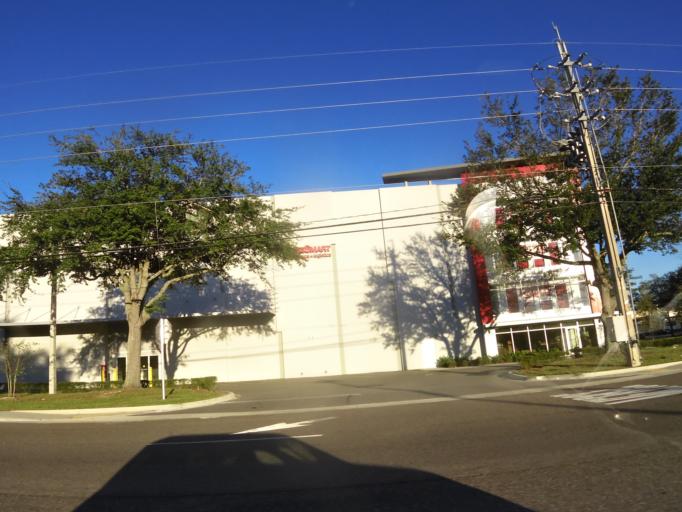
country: US
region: Florida
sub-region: Duval County
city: Jacksonville Beach
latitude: 30.2894
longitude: -81.4377
